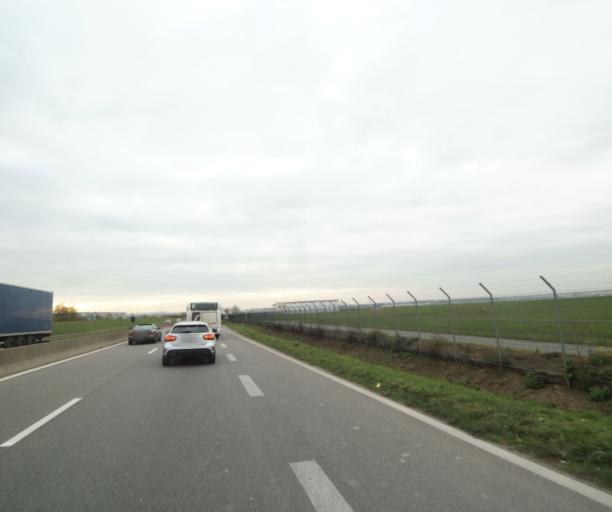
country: FR
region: Ile-de-France
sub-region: Departement du Val-d'Oise
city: Gonesse
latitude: 48.9708
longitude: 2.4580
